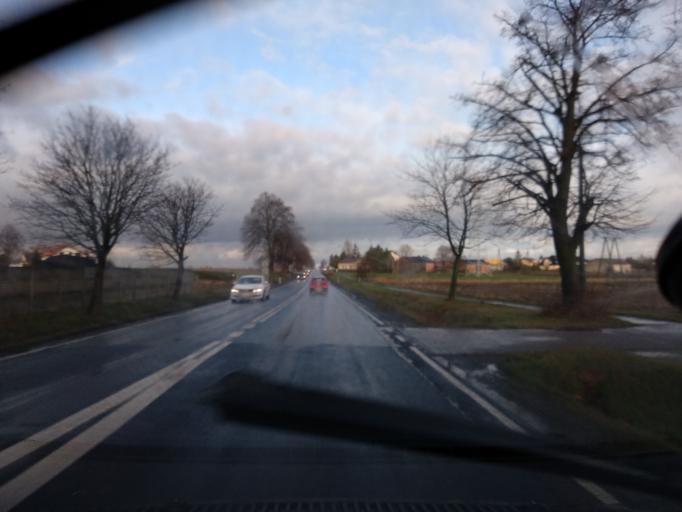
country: PL
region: Greater Poland Voivodeship
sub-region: Powiat koninski
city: Rychwal
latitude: 52.0793
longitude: 18.1606
